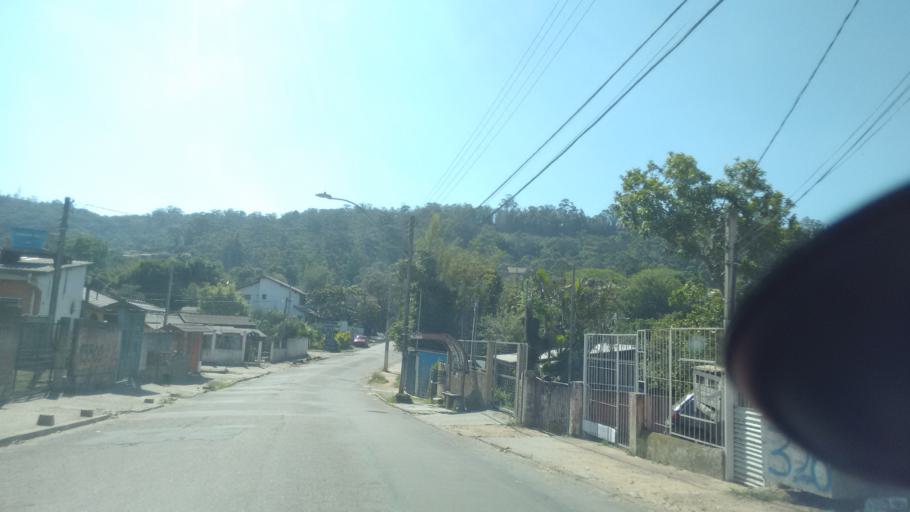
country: BR
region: Rio Grande do Sul
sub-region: Viamao
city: Viamao
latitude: -30.0574
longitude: -51.1028
